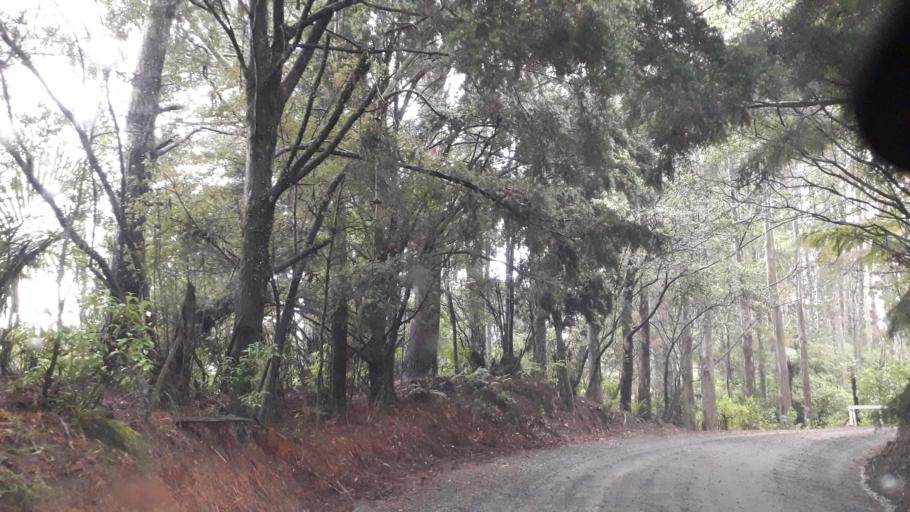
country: NZ
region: Northland
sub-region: Far North District
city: Kerikeri
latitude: -35.1186
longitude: 173.7512
